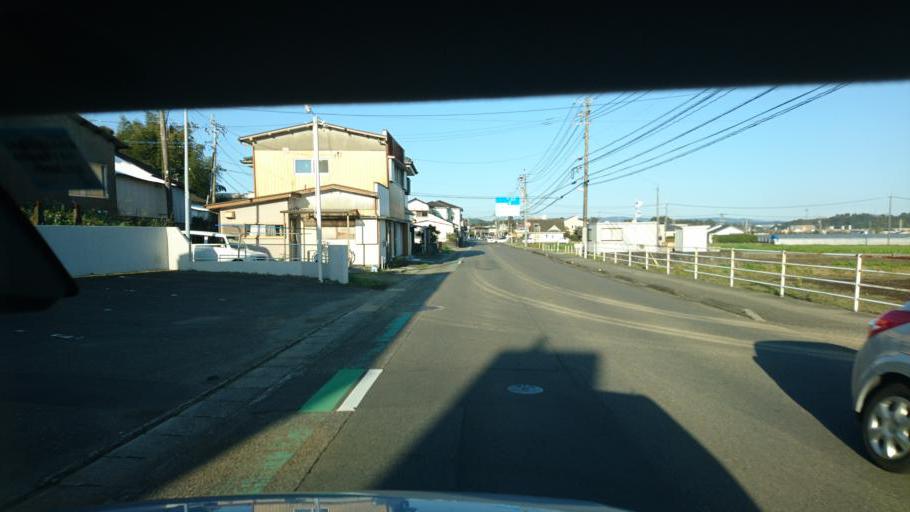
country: JP
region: Miyazaki
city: Miyazaki-shi
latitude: 31.8456
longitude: 131.3963
